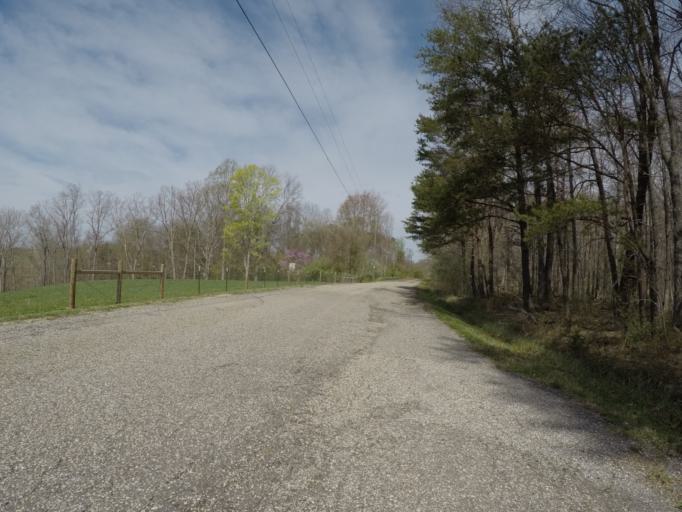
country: US
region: West Virginia
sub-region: Wayne County
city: Lavalette
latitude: 38.3296
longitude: -82.3593
